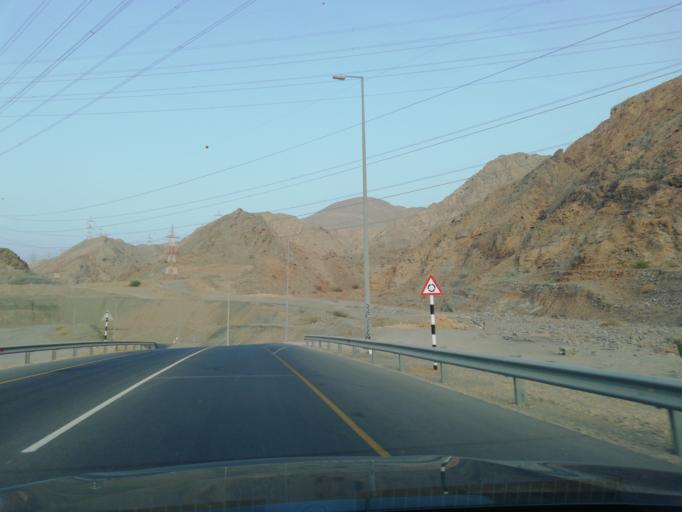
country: OM
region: Muhafazat Masqat
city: Bawshar
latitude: 23.5787
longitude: 58.4441
